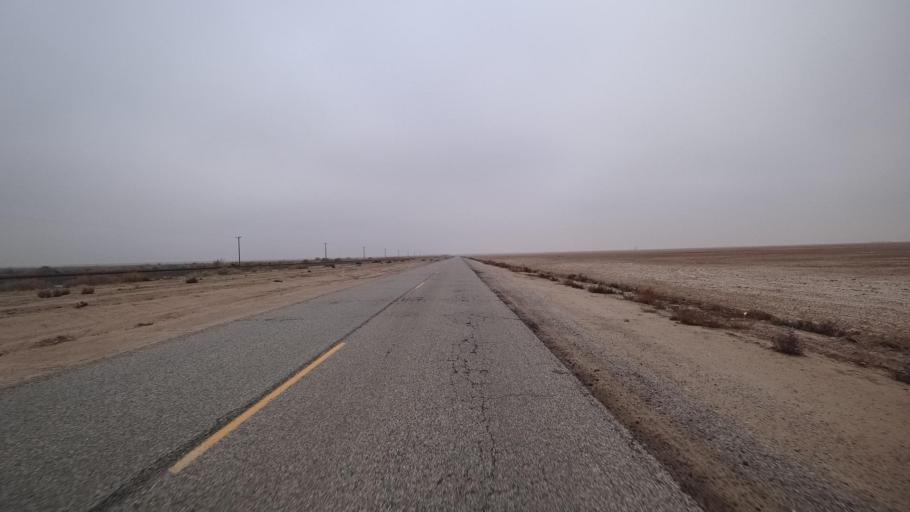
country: US
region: California
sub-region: Kern County
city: Maricopa
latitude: 35.1309
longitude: -119.2550
